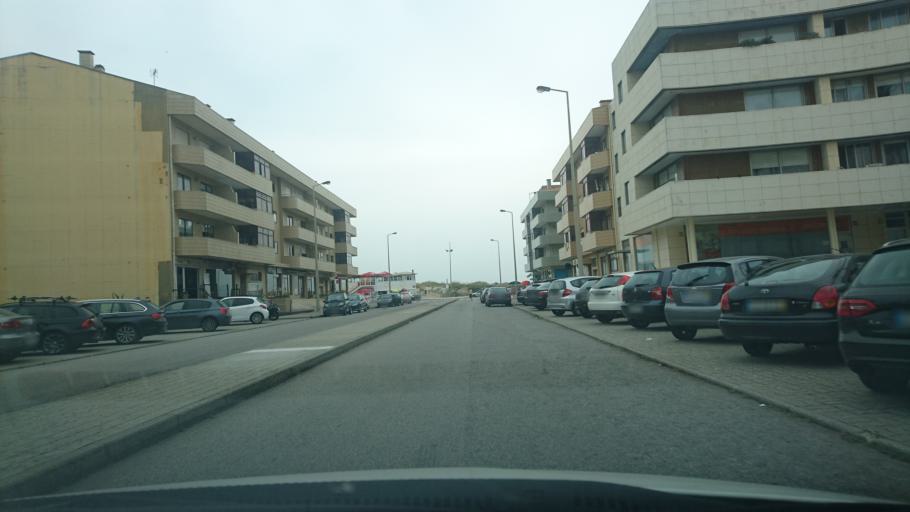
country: PT
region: Aveiro
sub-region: Ovar
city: Esmoriz
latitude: 40.9575
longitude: -8.6533
